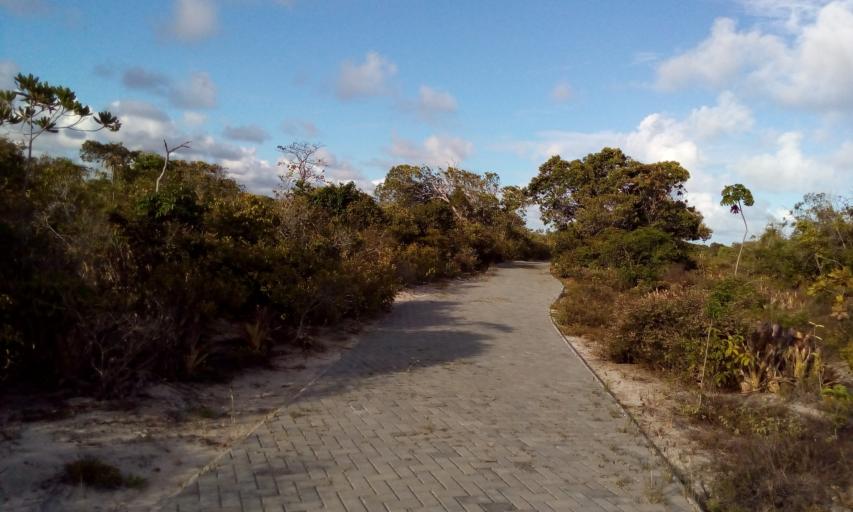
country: BR
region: Bahia
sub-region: Mata De Sao Joao
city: Mata de Sao Joao
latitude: -12.5654
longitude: -38.0039
